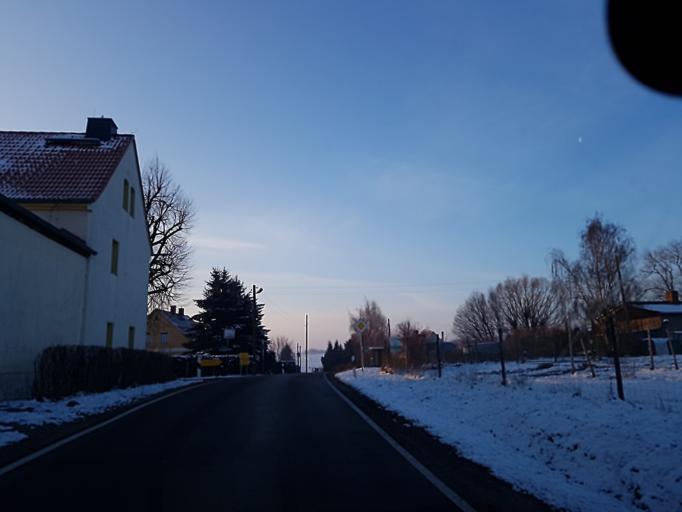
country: DE
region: Saxony
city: Mugeln
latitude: 51.2080
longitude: 13.0308
